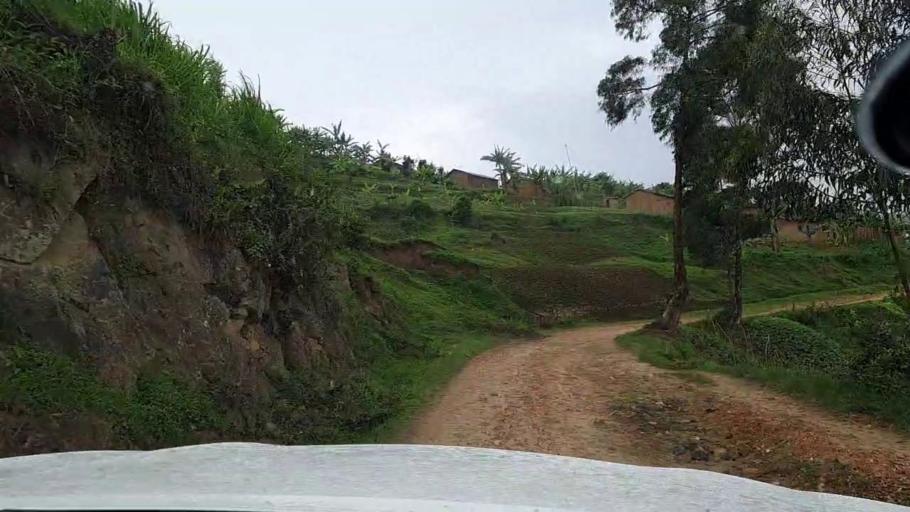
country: RW
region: Western Province
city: Kibuye
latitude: -2.0782
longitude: 29.4446
